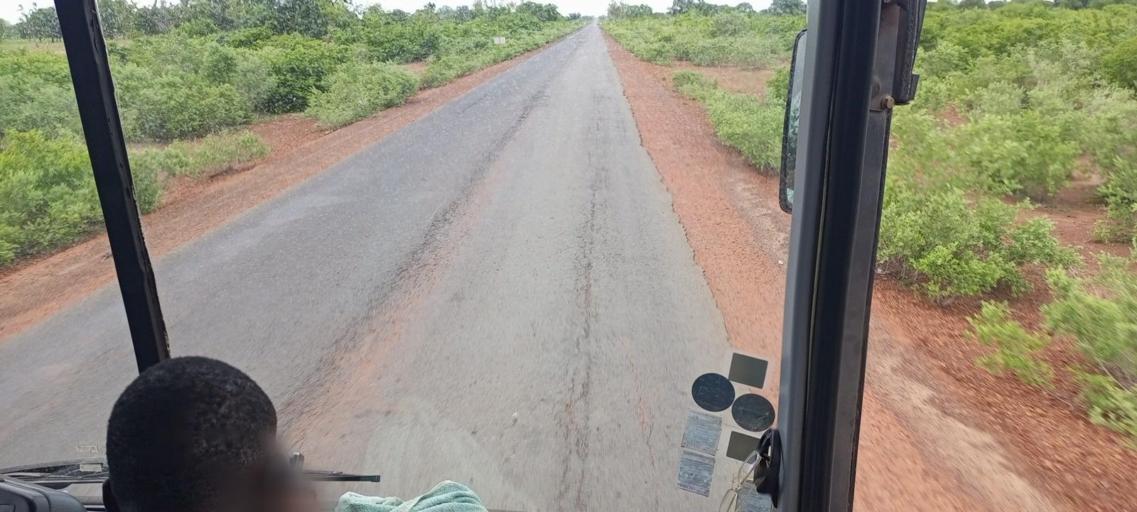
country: ML
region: Sikasso
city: Koutiala
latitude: 12.5602
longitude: -5.5927
